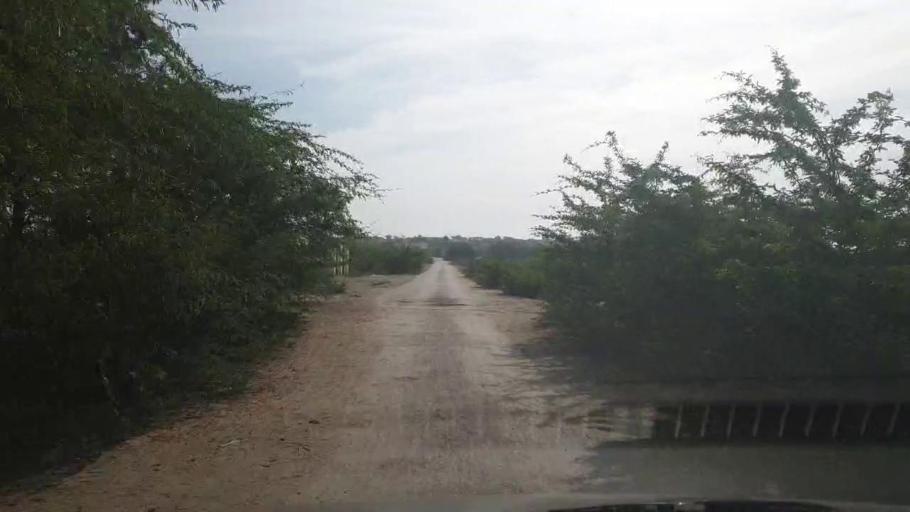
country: PK
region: Sindh
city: Umarkot
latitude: 25.3017
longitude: 69.7157
